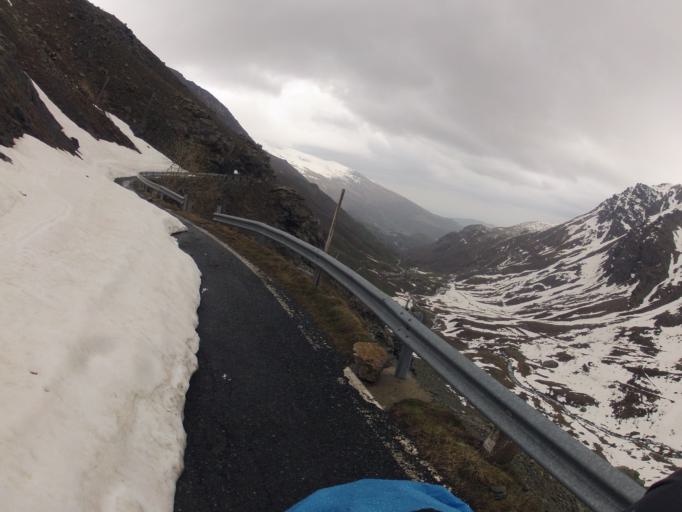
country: IT
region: Piedmont
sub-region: Provincia di Cuneo
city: Crissolo
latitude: 44.7002
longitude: 7.1022
